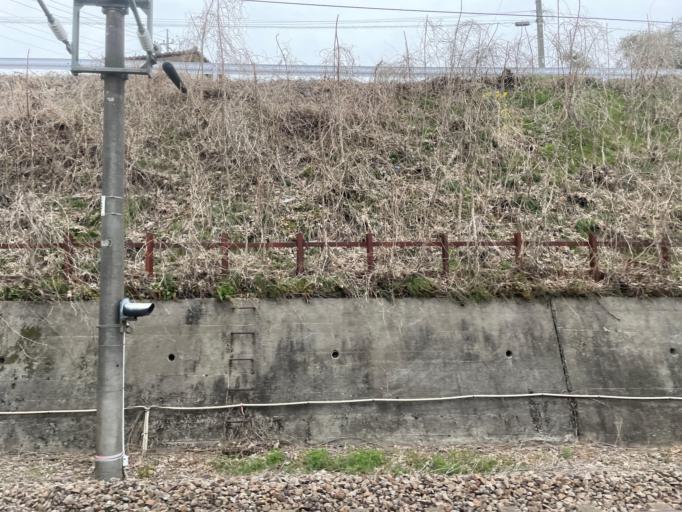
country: JP
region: Gunma
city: Numata
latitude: 36.5567
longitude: 139.0447
